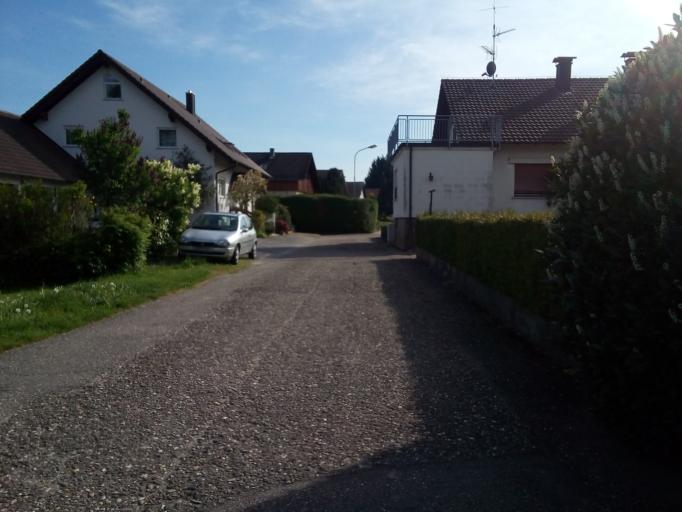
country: DE
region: Baden-Wuerttemberg
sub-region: Karlsruhe Region
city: Lichtenau
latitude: 48.7249
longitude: 8.0123
